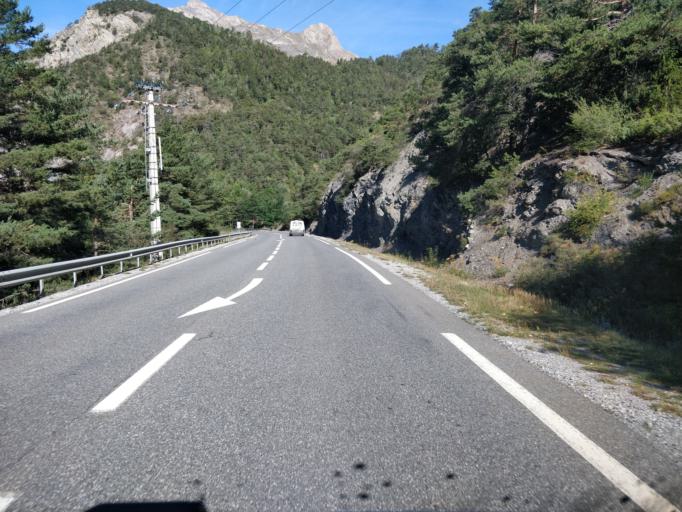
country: FR
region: Provence-Alpes-Cote d'Azur
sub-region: Departement des Alpes-de-Haute-Provence
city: Barcelonnette
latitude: 44.4006
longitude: 6.5292
